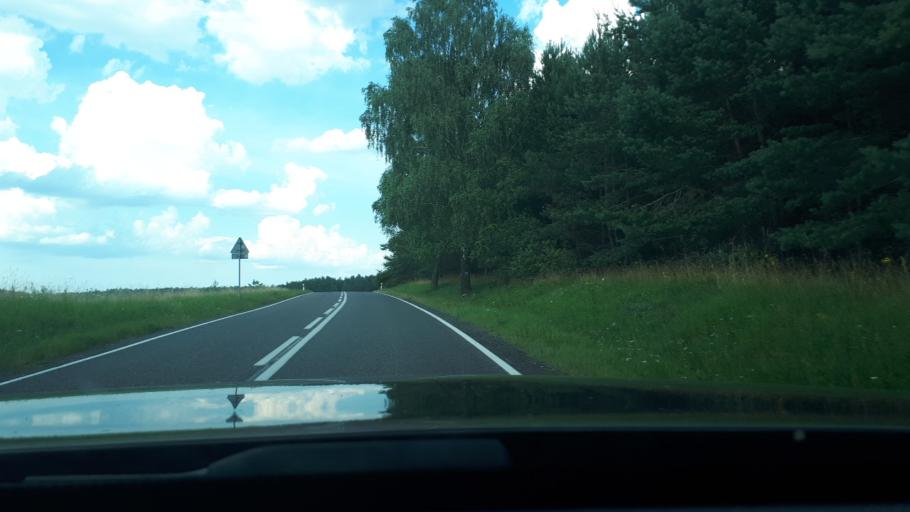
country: PL
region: Warmian-Masurian Voivodeship
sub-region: Powiat olsztynski
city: Stawiguda
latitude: 53.5376
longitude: 20.4845
